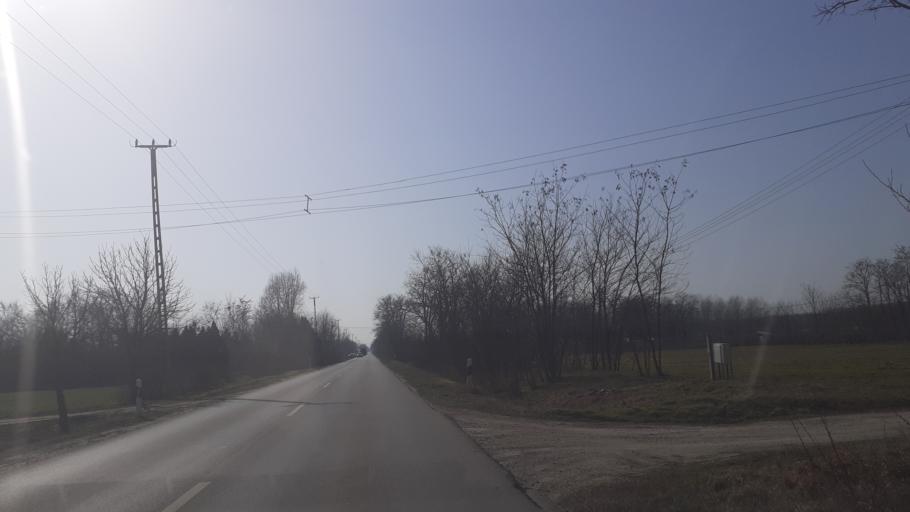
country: HU
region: Bacs-Kiskun
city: Lajosmizse
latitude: 47.0155
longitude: 19.5158
